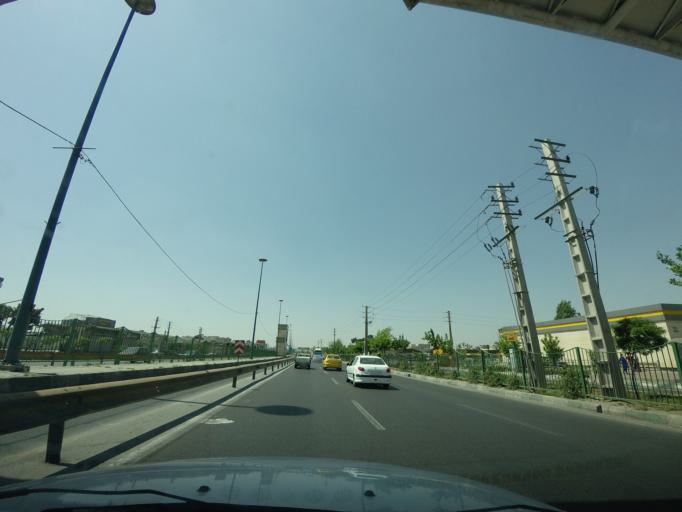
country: IR
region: Tehran
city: Tehran
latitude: 35.6339
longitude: 51.3472
